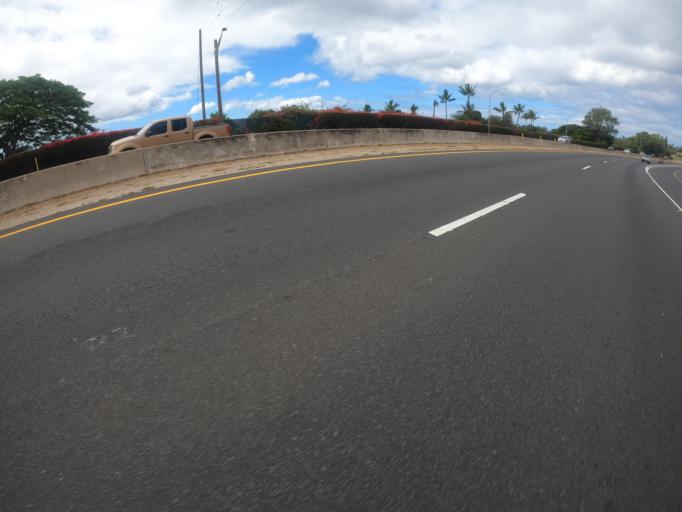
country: US
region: Hawaii
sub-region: Honolulu County
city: Makakilo City
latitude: 21.3444
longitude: -158.1196
